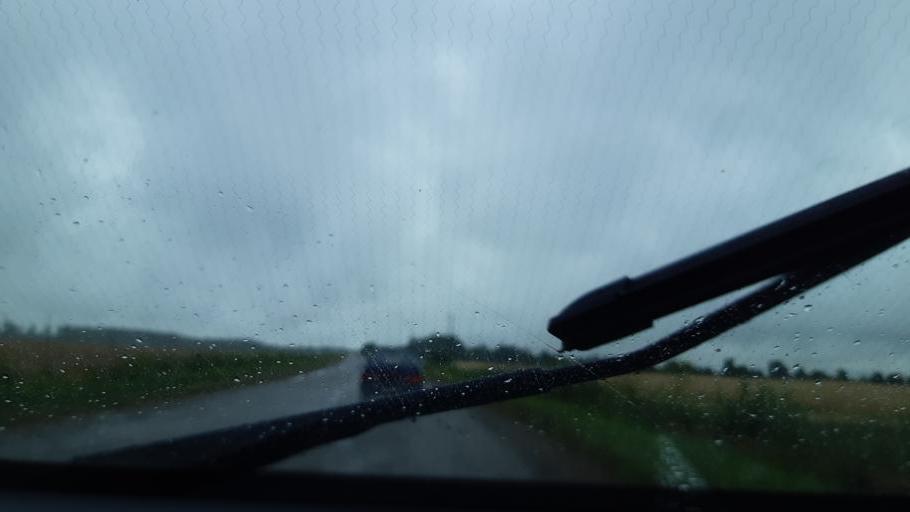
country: RU
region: Smolensk
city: Gagarin
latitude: 55.6362
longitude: 34.7560
